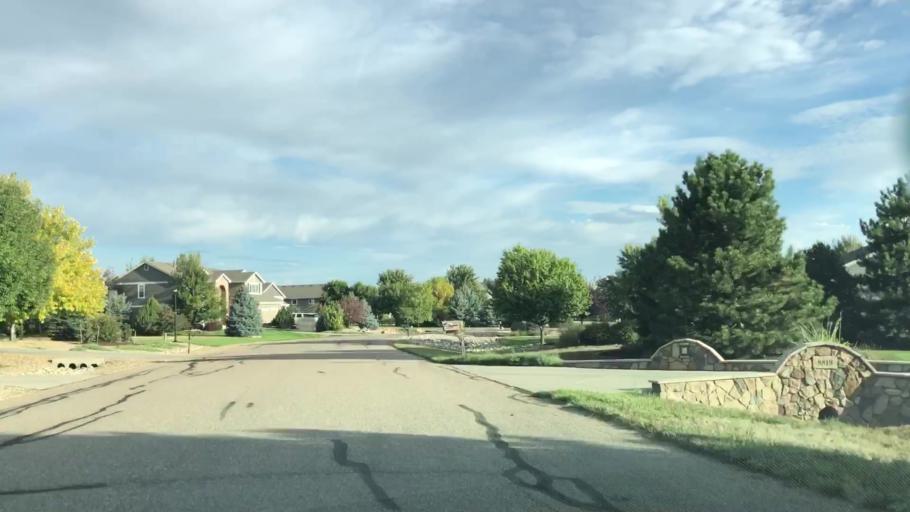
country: US
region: Colorado
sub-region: Weld County
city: Windsor
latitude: 40.4396
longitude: -104.9617
